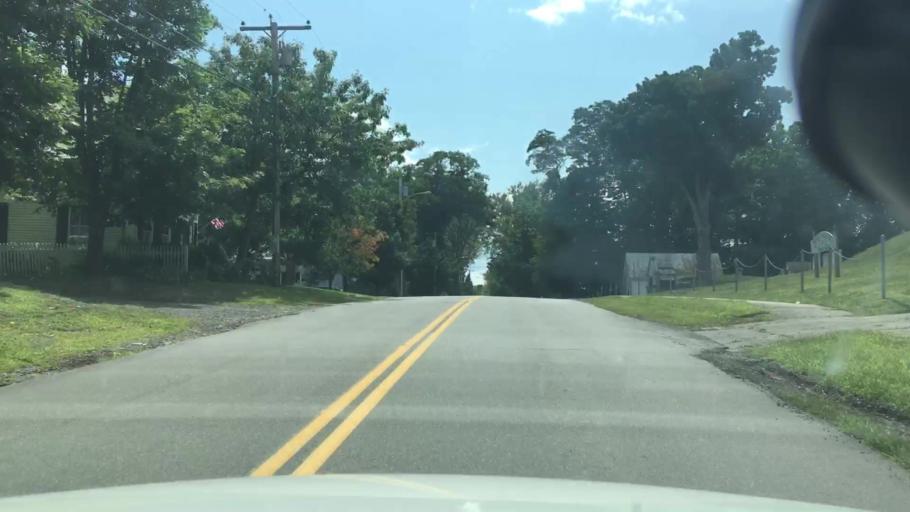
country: US
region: Maine
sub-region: Somerset County
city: Skowhegan
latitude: 44.7564
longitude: -69.7170
